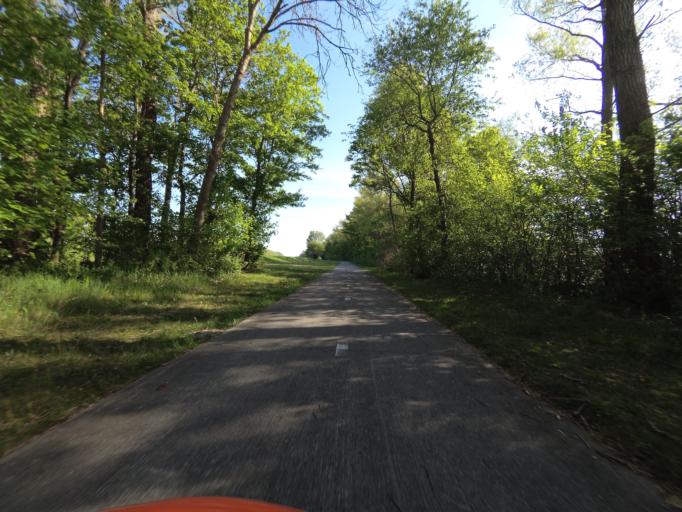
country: NL
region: Gelderland
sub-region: Gemeente Elburg
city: Elburg
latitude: 52.4393
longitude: 5.7954
